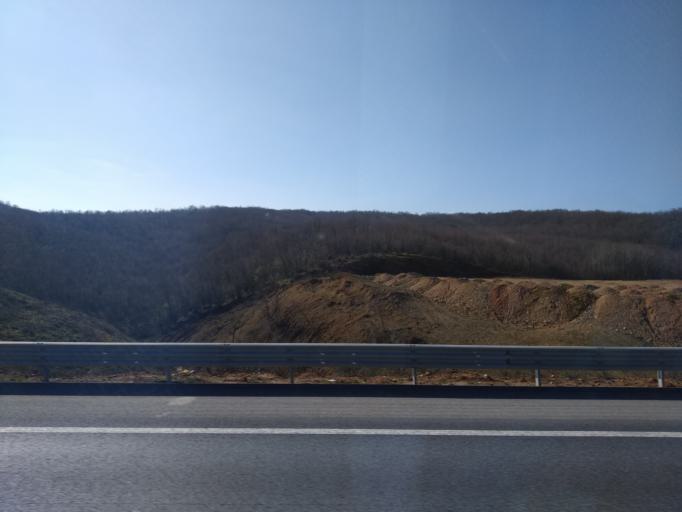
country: TR
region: Istanbul
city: Mahmut Sevket Pasa
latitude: 41.1634
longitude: 29.2568
